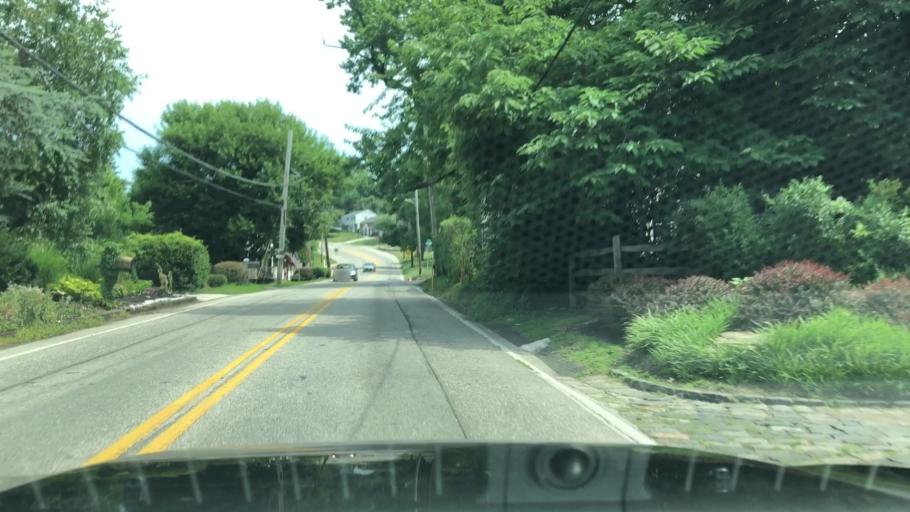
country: US
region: Pennsylvania
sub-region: Montgomery County
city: Norristown
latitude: 40.1139
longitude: -75.3080
